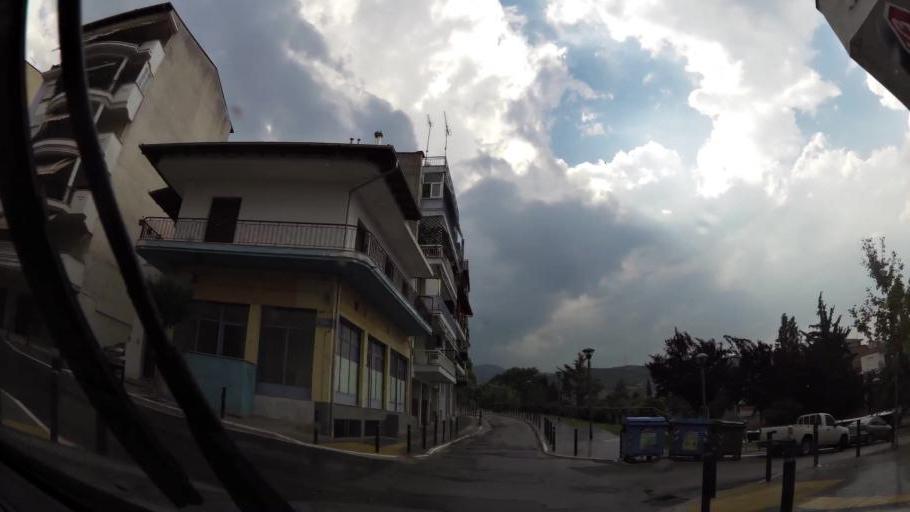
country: GR
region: Central Macedonia
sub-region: Nomos Imathias
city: Veroia
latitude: 40.5306
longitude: 22.2021
